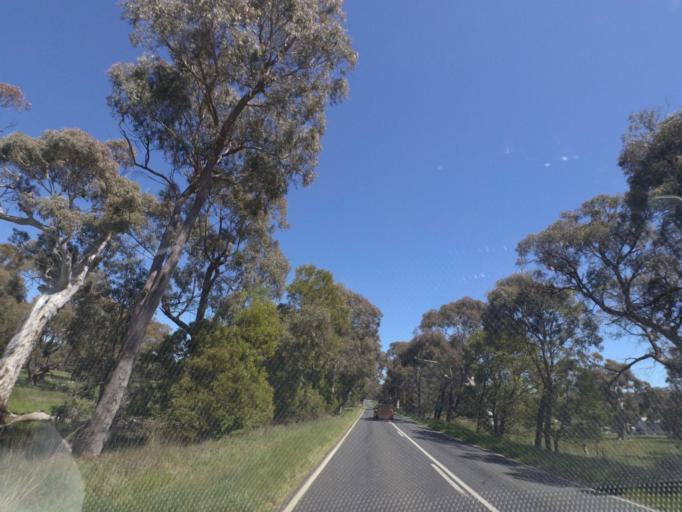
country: AU
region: Victoria
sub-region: Hume
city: Sunbury
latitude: -37.3140
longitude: 144.6609
